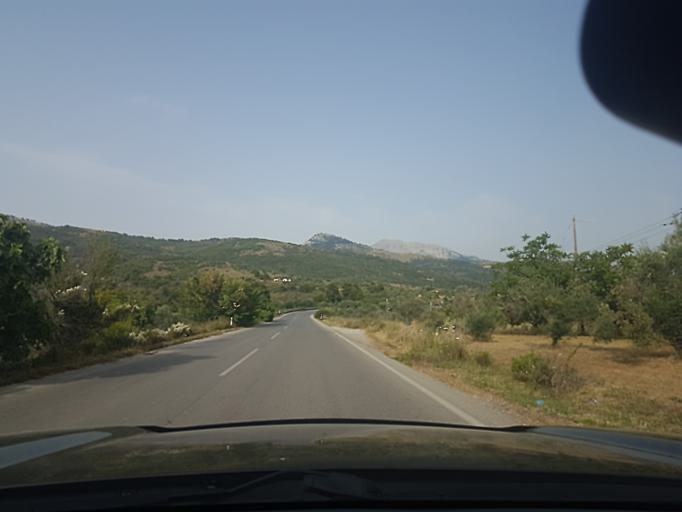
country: GR
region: Central Greece
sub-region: Nomos Evvoias
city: Yimnon
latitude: 38.5758
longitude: 23.8085
